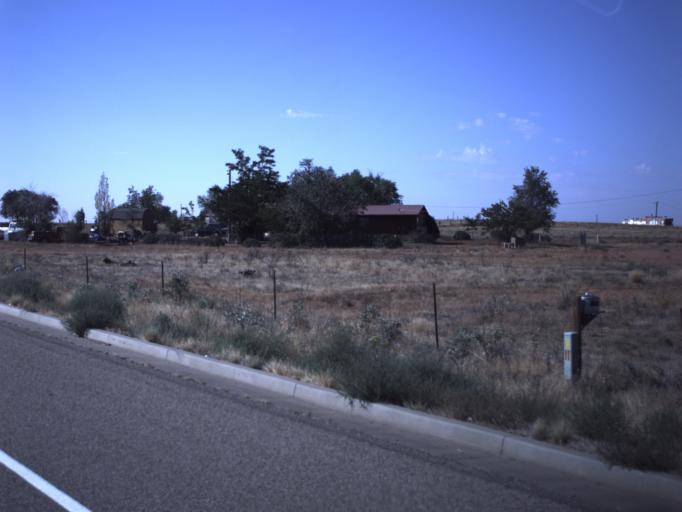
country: US
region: Utah
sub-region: San Juan County
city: Blanding
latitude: 37.4621
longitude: -109.4671
